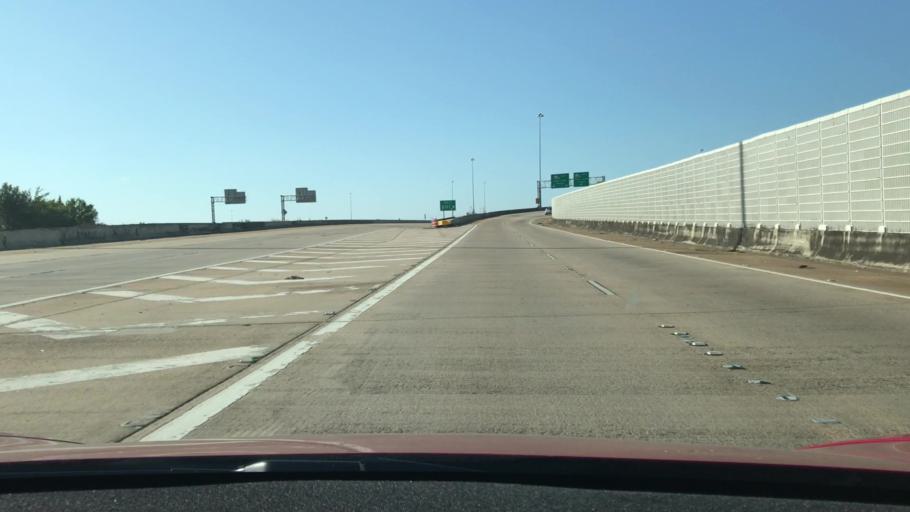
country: US
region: Louisiana
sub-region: Bossier Parish
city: Bossier City
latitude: 32.4250
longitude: -93.7509
